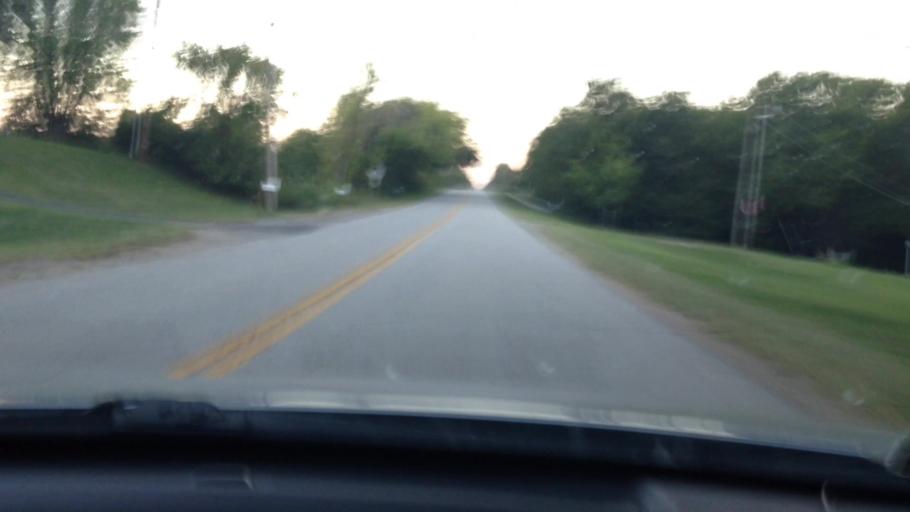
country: US
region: Kansas
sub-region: Leavenworth County
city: Lansing
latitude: 39.1833
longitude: -94.8267
